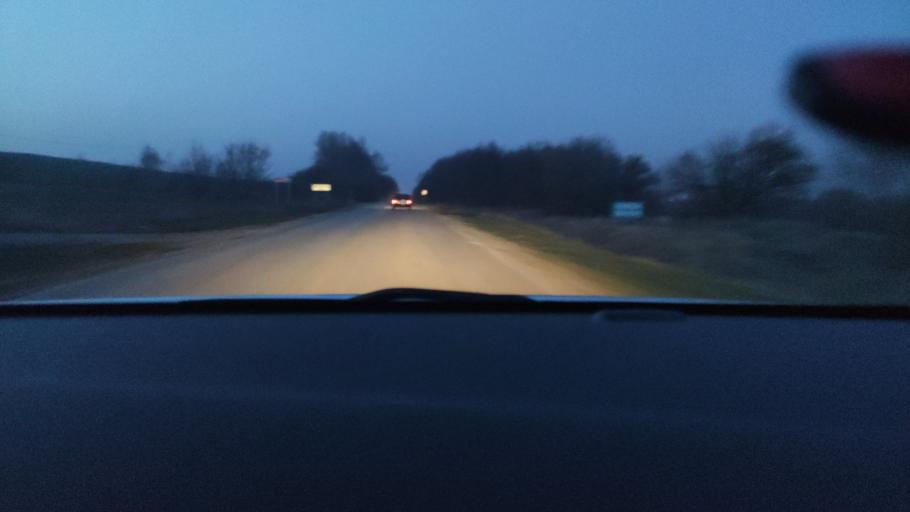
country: RU
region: Voronezj
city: Shilovo
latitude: 51.5140
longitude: 39.0155
